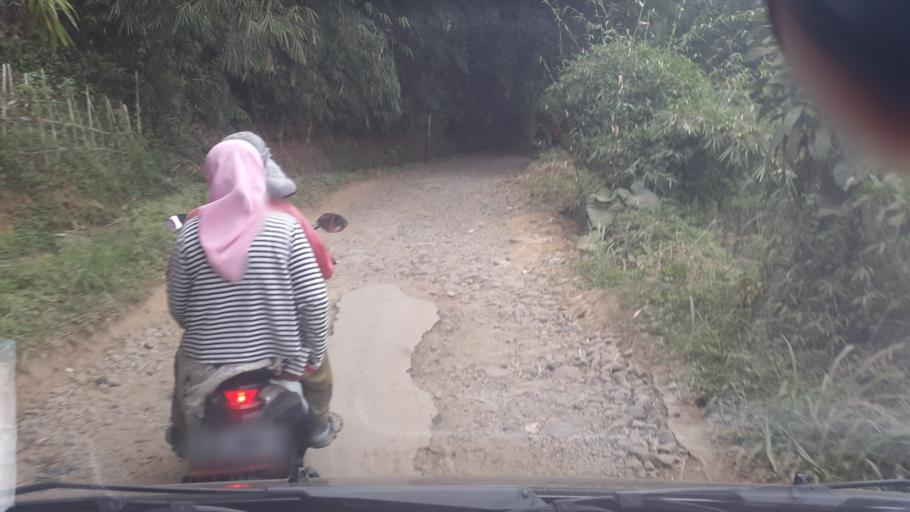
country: ID
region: West Java
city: Sukabumi
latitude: -6.8619
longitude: 106.8881
